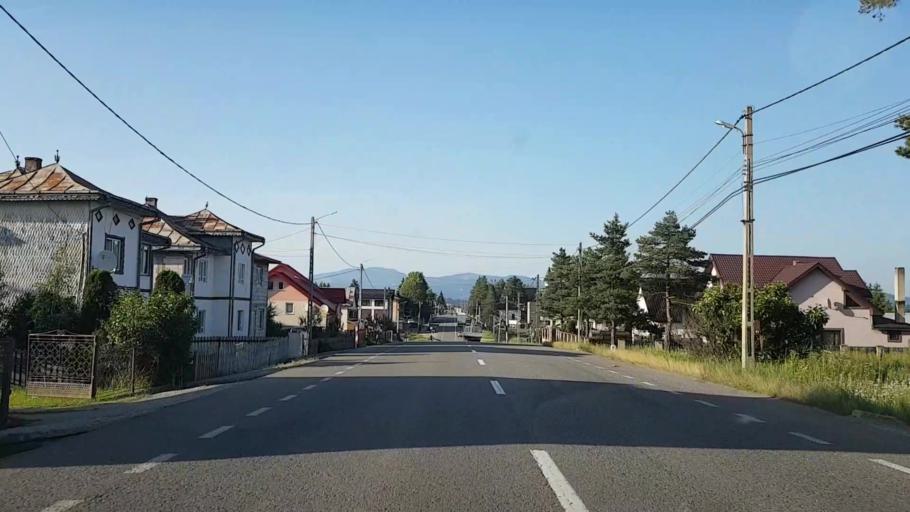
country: RO
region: Suceava
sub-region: Comuna Poiana Stampei
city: Poiana Stampei
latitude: 47.3176
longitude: 25.1343
